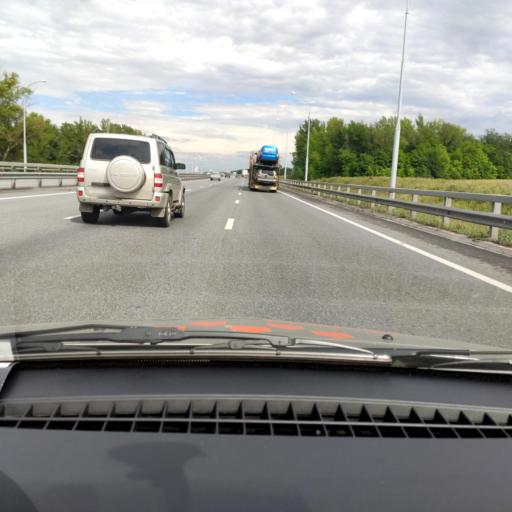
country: RU
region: Bashkortostan
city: Kabakovo
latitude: 54.6515
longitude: 56.1000
